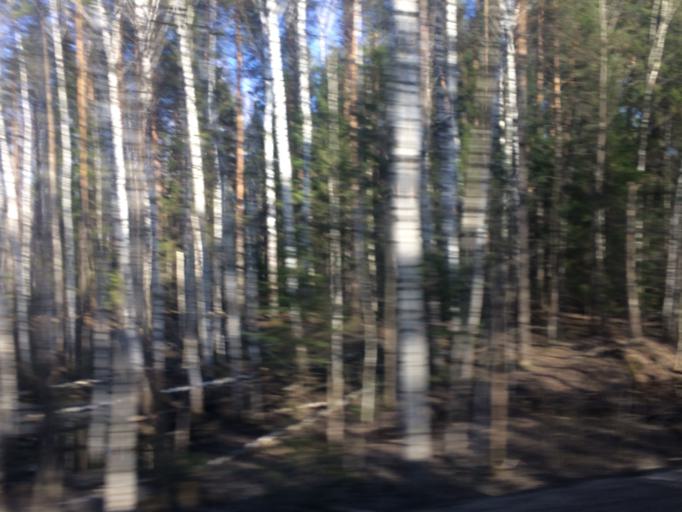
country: RU
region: Tatarstan
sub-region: Zelenodol'skiy Rayon
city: Vasil'yevo
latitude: 55.8936
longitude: 48.7284
